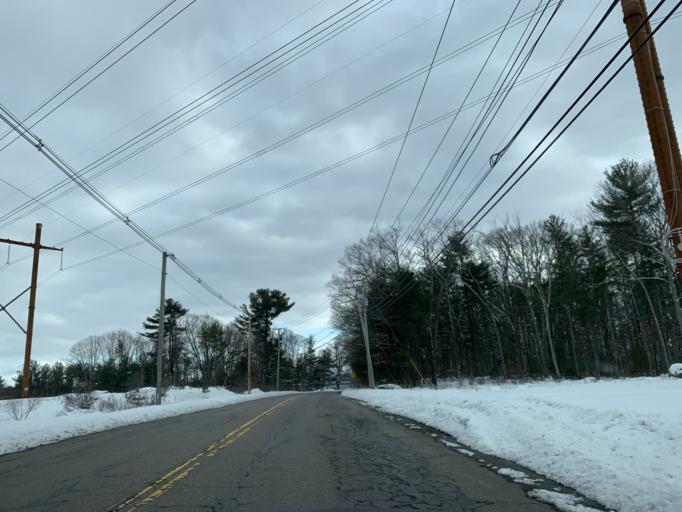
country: US
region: Massachusetts
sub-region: Norfolk County
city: Franklin
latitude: 42.0739
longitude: -71.4235
